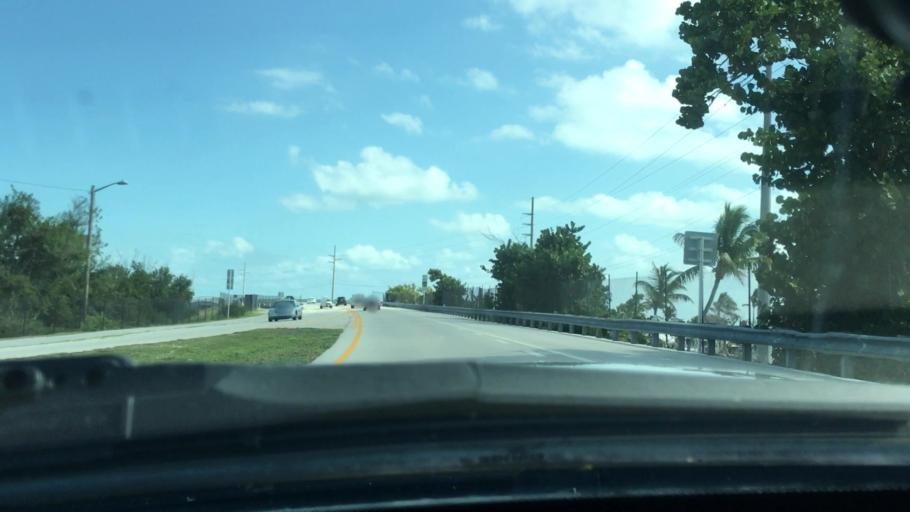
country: US
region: Florida
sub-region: Monroe County
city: Big Pine Key
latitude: 24.6483
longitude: -81.3311
